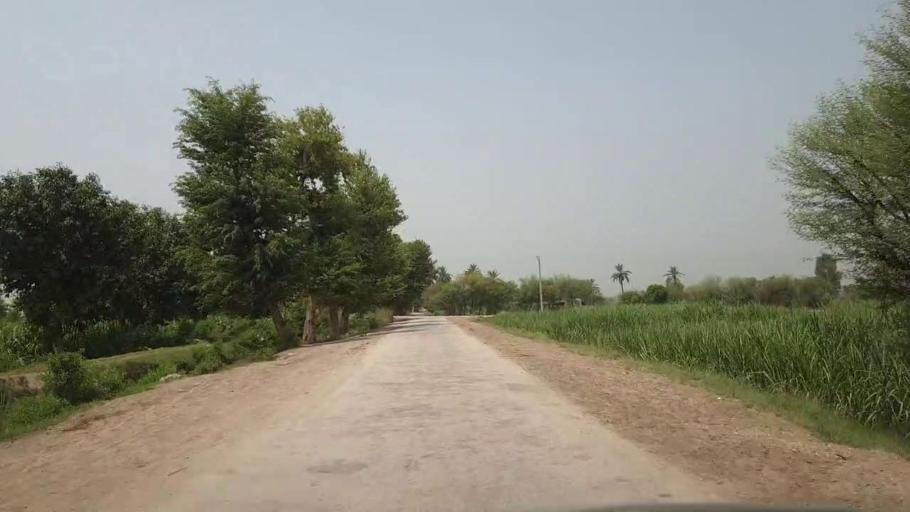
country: PK
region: Sindh
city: Gambat
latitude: 27.4386
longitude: 68.4888
